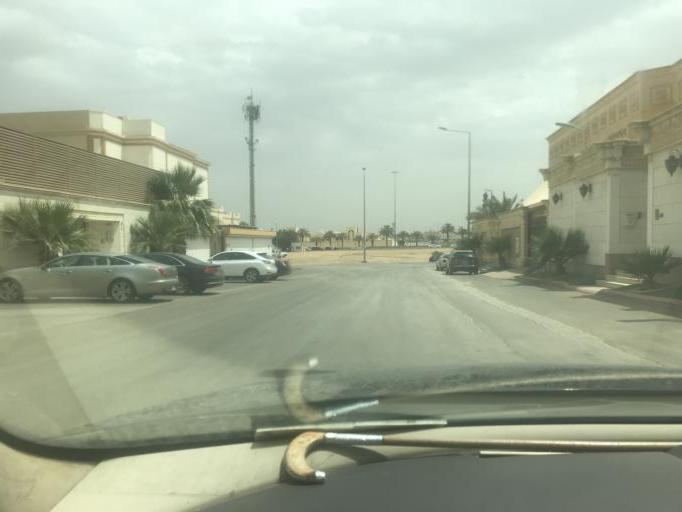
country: SA
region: Ar Riyad
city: Riyadh
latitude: 24.7921
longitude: 46.7156
